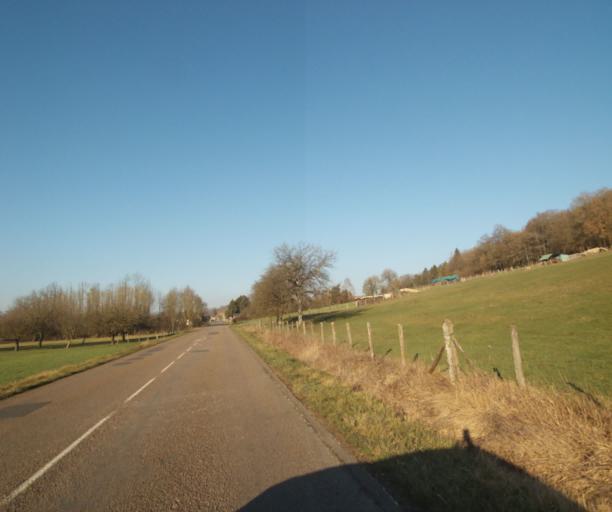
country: FR
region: Champagne-Ardenne
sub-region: Departement de la Haute-Marne
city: Chevillon
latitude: 48.5342
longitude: 5.1064
